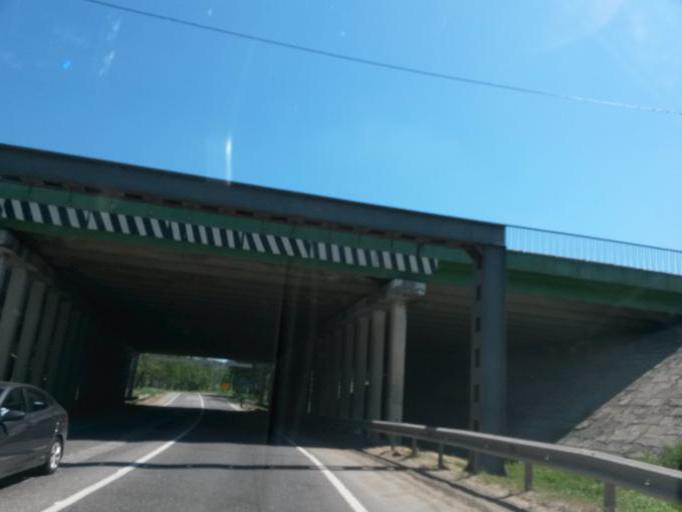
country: RU
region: Moskovskaya
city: Danki
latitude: 54.9060
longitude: 37.5112
